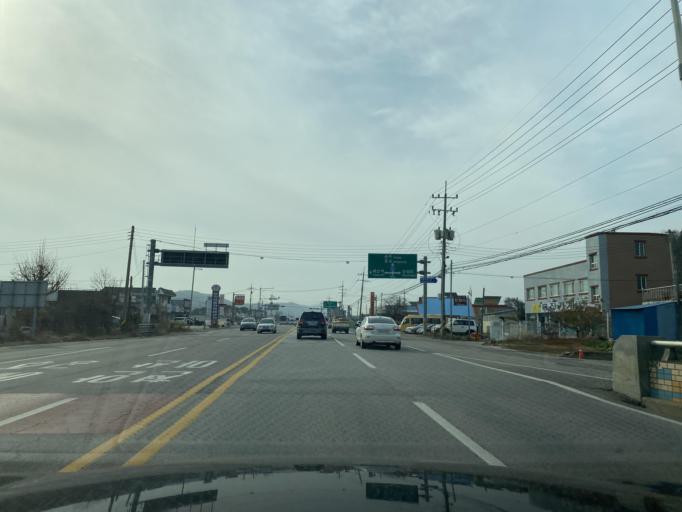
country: KR
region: Chungcheongnam-do
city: Yesan
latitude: 36.6925
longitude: 126.8280
